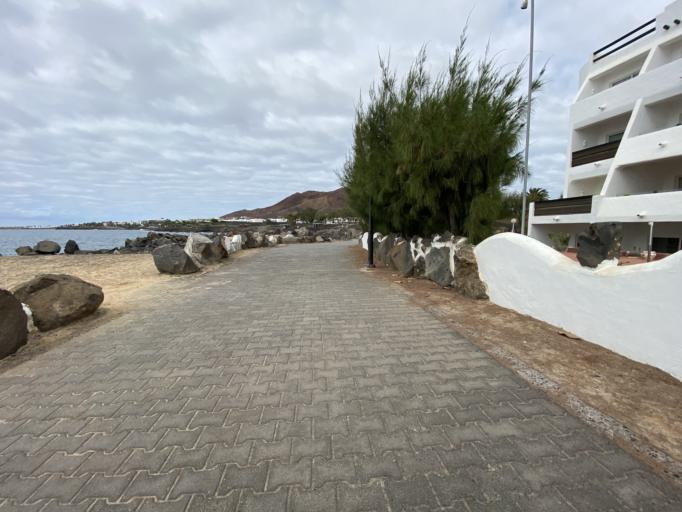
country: ES
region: Canary Islands
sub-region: Provincia de Las Palmas
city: Playa Blanca
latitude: 28.8603
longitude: -13.8459
